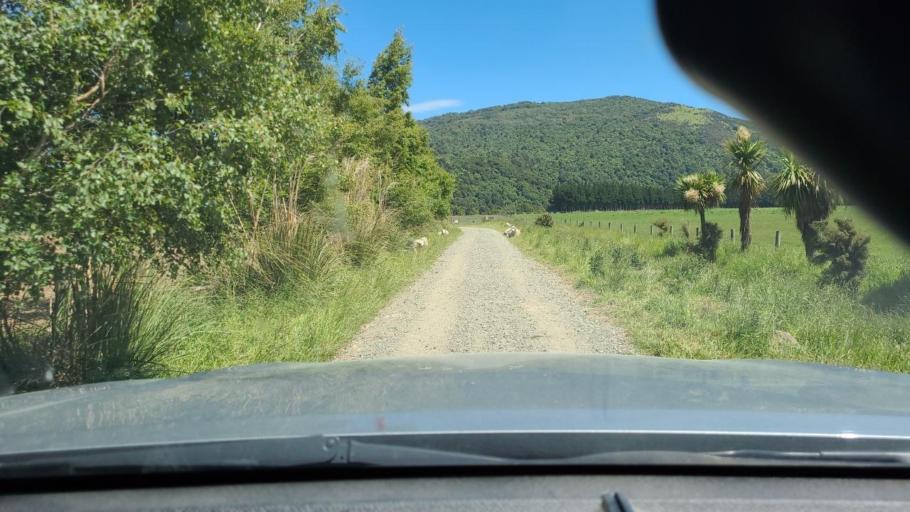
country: NZ
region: Southland
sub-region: Southland District
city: Te Anau
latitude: -45.8437
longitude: 167.6571
